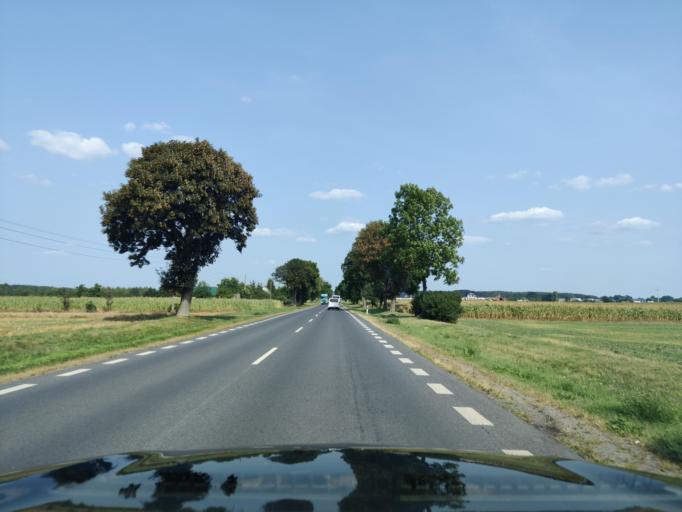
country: PL
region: Masovian Voivodeship
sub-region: Powiat makowski
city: Szelkow
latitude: 52.8435
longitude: 21.2669
